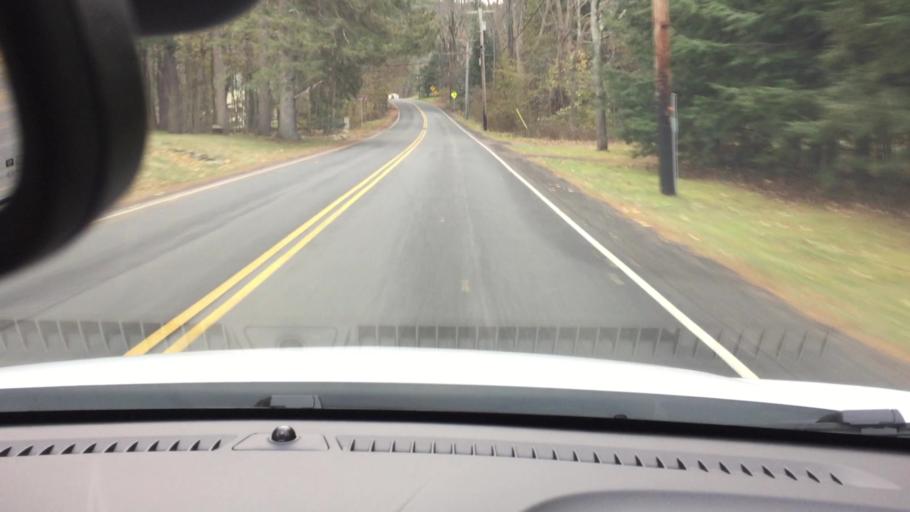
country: US
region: Massachusetts
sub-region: Berkshire County
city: New Marlborough
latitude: 42.1747
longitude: -73.1929
